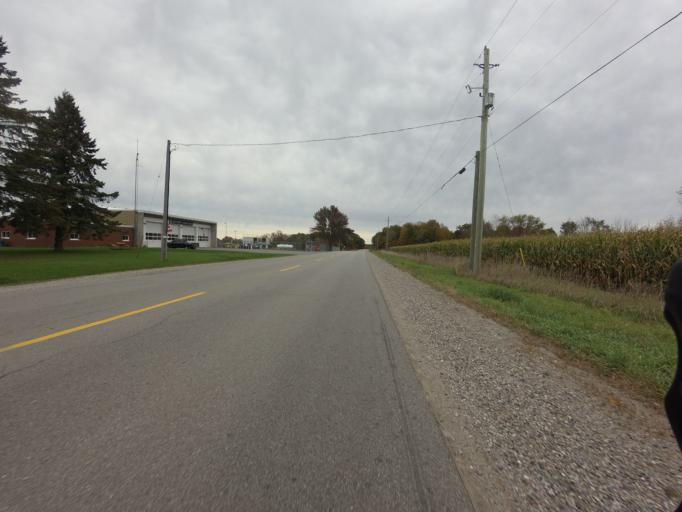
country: CA
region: Ontario
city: Gananoque
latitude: 44.5341
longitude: -76.1463
